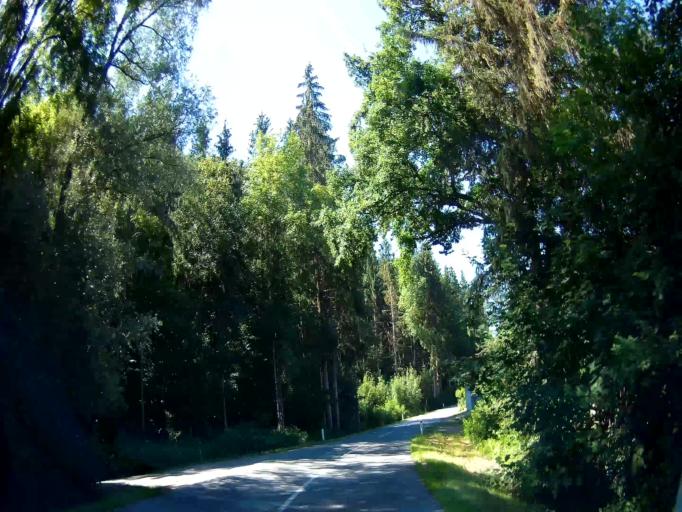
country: AT
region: Carinthia
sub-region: Politischer Bezirk Klagenfurt Land
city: Grafenstein
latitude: 46.6048
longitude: 14.4424
